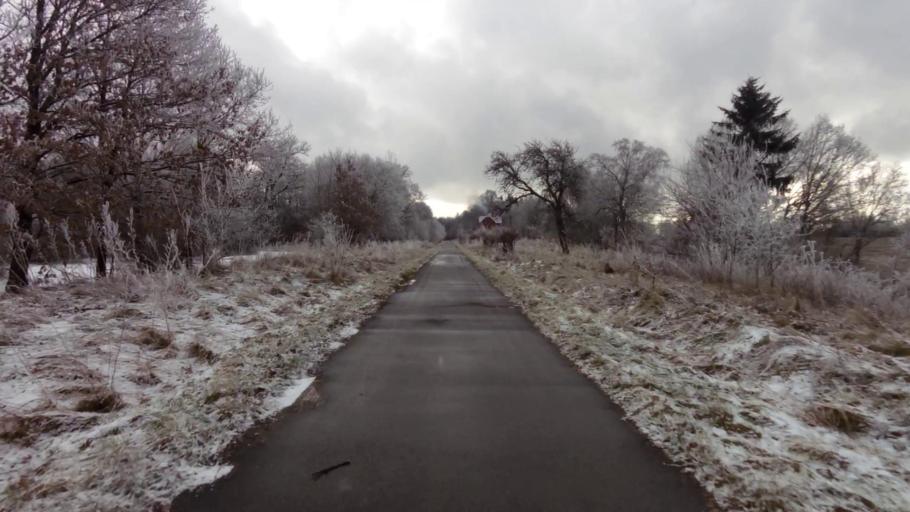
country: PL
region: West Pomeranian Voivodeship
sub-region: Powiat swidwinski
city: Polczyn-Zdroj
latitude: 53.6679
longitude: 16.0306
